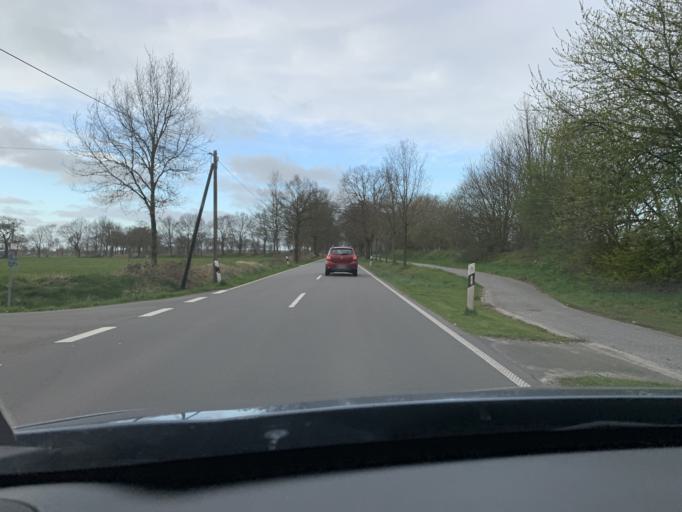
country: DE
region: Lower Saxony
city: Schwerinsdorf
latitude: 53.2631
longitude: 7.7082
